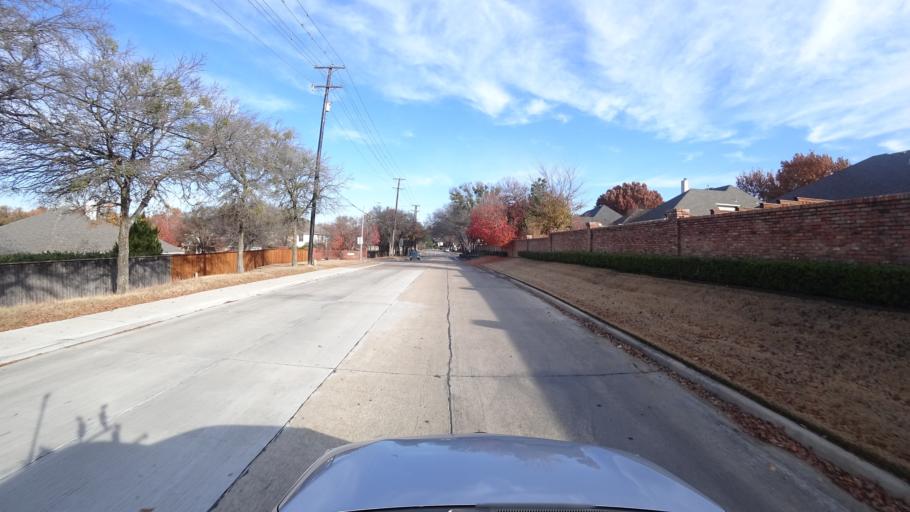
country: US
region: Texas
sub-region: Collin County
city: McKinney
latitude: 33.2036
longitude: -96.6546
